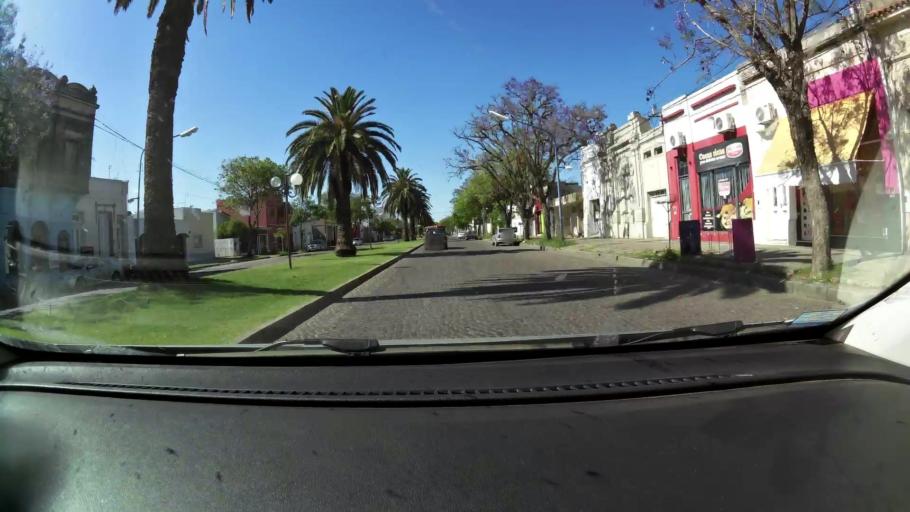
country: AR
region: Santa Fe
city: Rafaela
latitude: -31.2466
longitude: -61.4902
